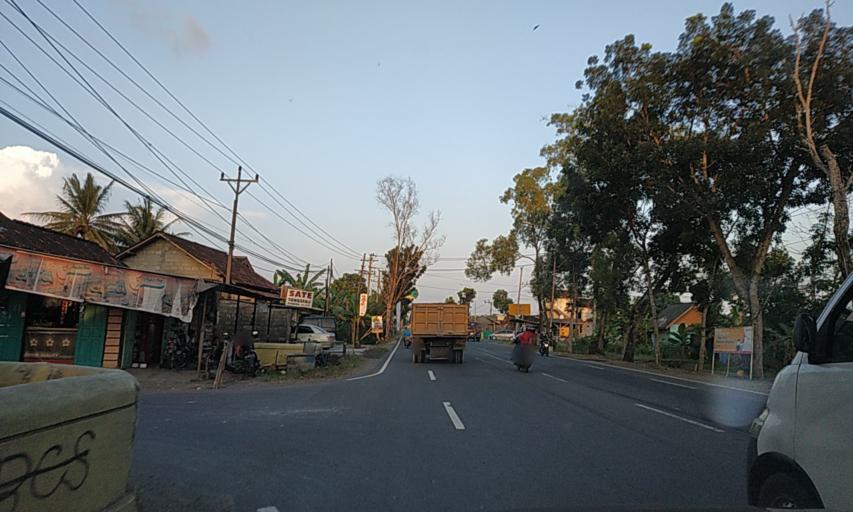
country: ID
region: Daerah Istimewa Yogyakarta
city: Srandakan
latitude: -7.8879
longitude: 110.0918
